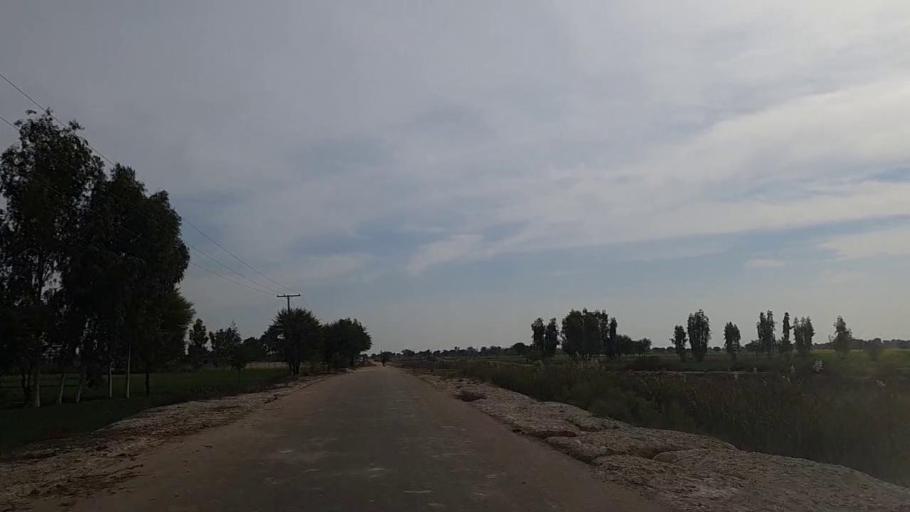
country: PK
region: Sindh
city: Daur
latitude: 26.4250
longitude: 68.4837
